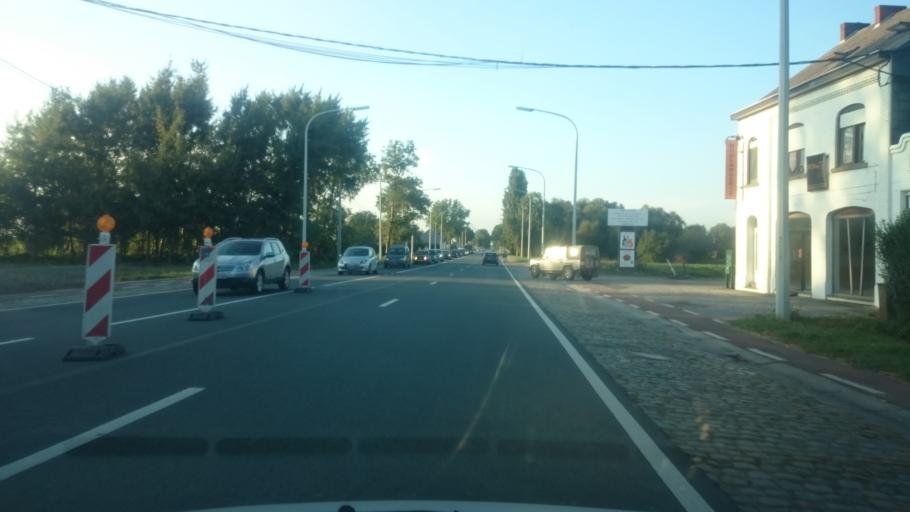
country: BE
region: Wallonia
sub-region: Province du Brabant Wallon
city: Chastre-Villeroux-Blanmont
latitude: 50.6144
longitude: 4.6650
